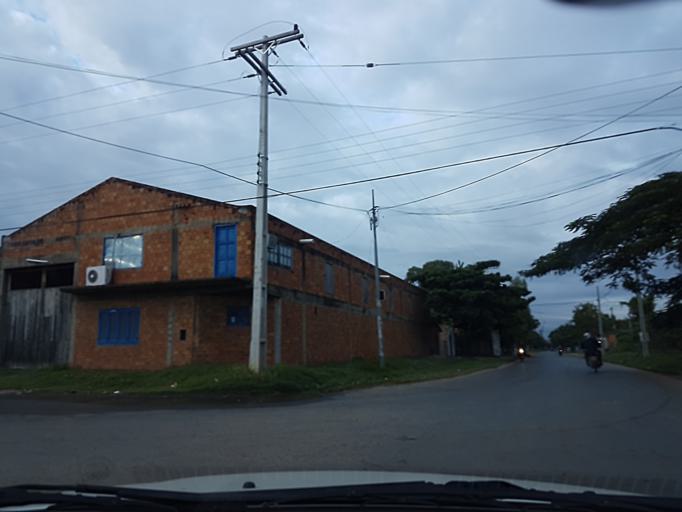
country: PY
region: Central
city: Colonia Mariano Roque Alonso
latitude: -25.2148
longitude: -57.5366
